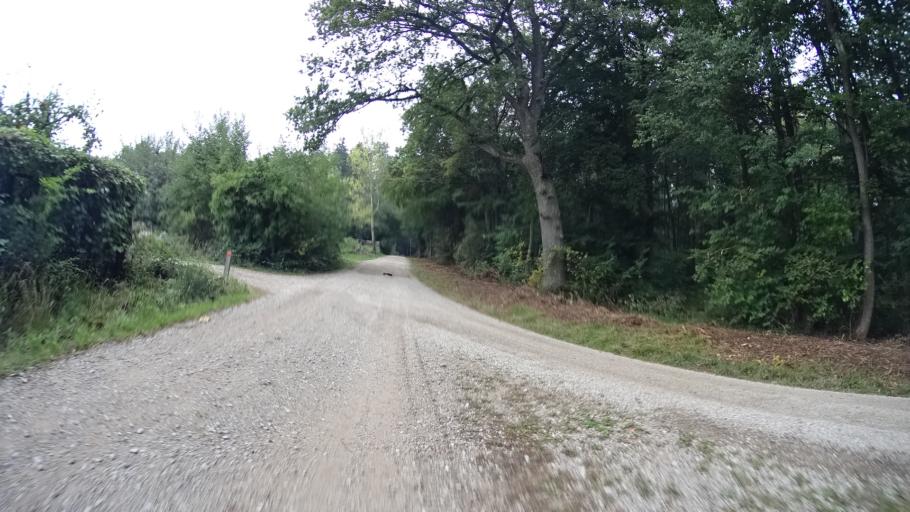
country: DE
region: Bavaria
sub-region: Upper Bavaria
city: Hepberg
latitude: 48.8321
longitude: 11.4893
